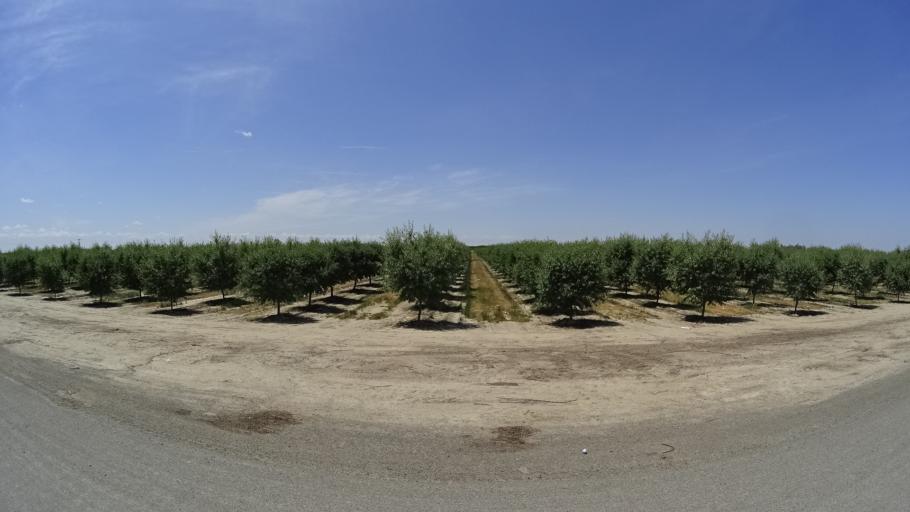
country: US
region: California
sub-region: Kings County
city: Home Garden
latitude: 36.2719
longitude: -119.6550
